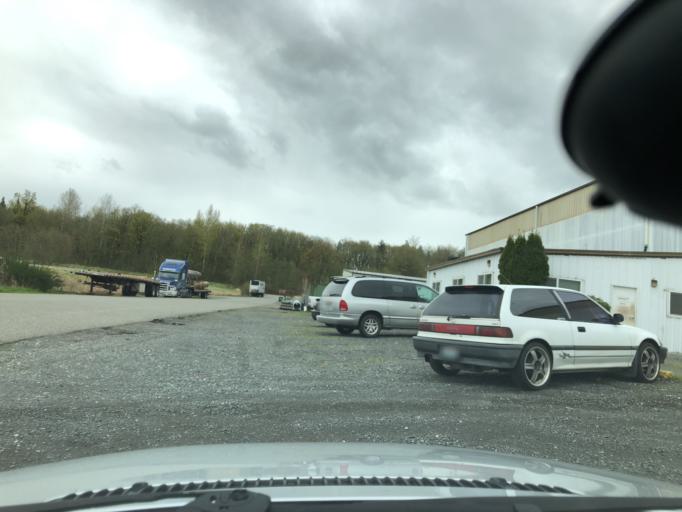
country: US
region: Washington
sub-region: Whatcom County
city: Ferndale
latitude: 48.8906
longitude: -122.6044
